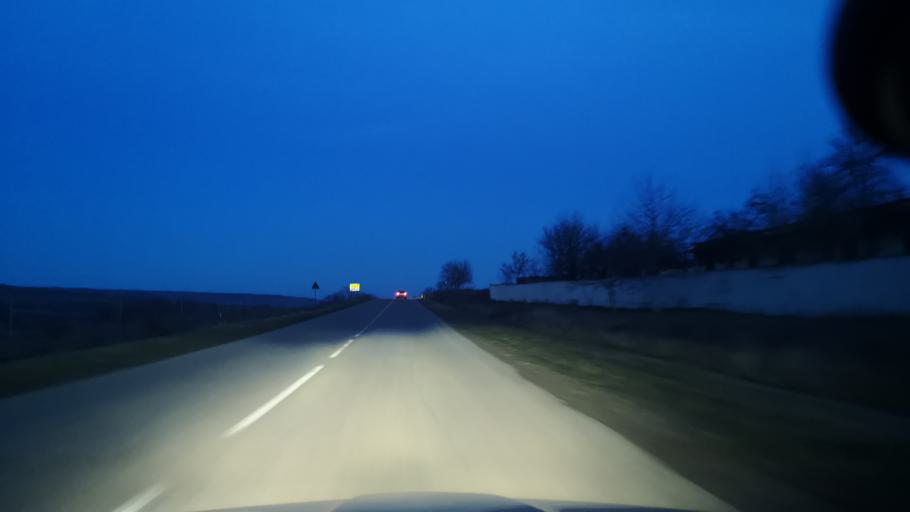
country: MD
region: Orhei
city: Orhei
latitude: 47.3400
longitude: 28.6590
